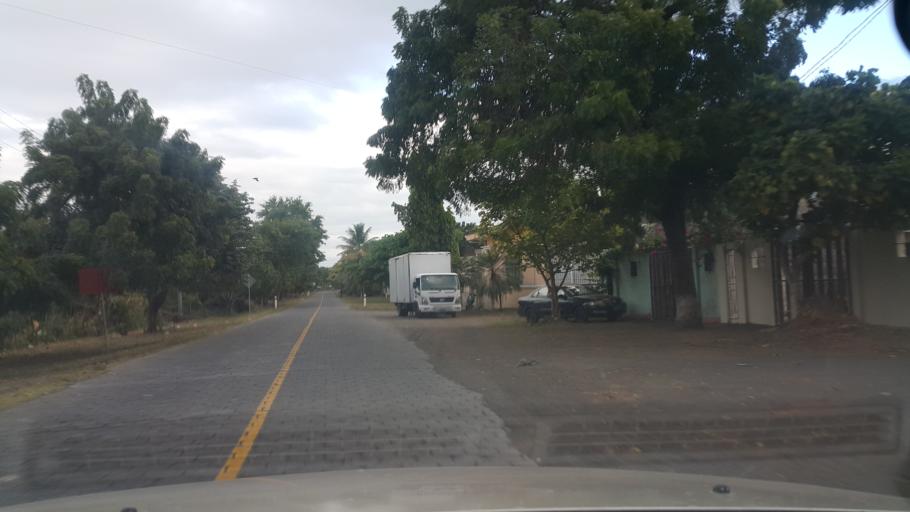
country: NI
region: Rivas
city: Moyogalpa
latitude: 11.5322
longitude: -85.6983
